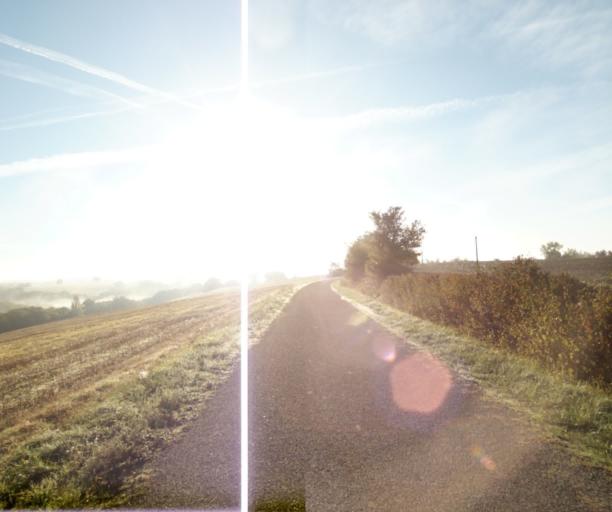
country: FR
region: Midi-Pyrenees
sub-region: Departement de la Haute-Garonne
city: Villemur-sur-Tarn
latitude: 43.8962
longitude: 1.4809
